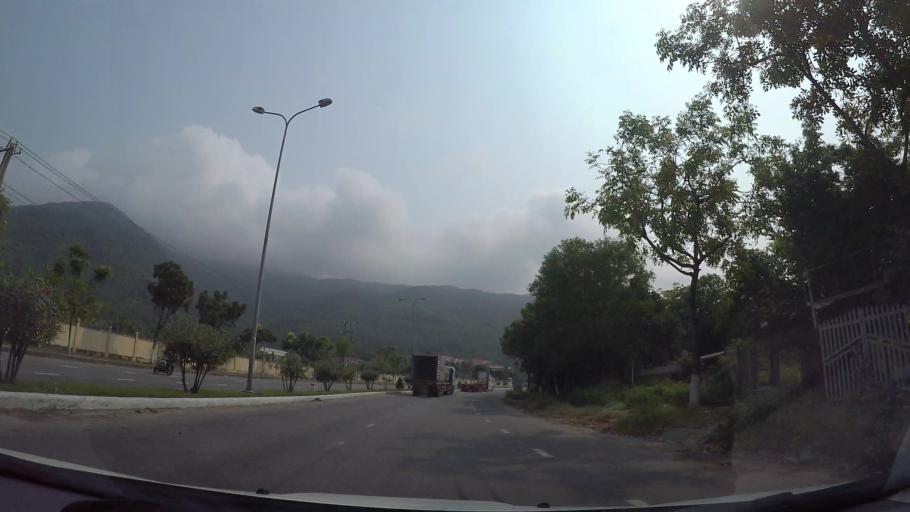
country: VN
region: Da Nang
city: Da Nang
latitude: 16.1143
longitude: 108.2386
